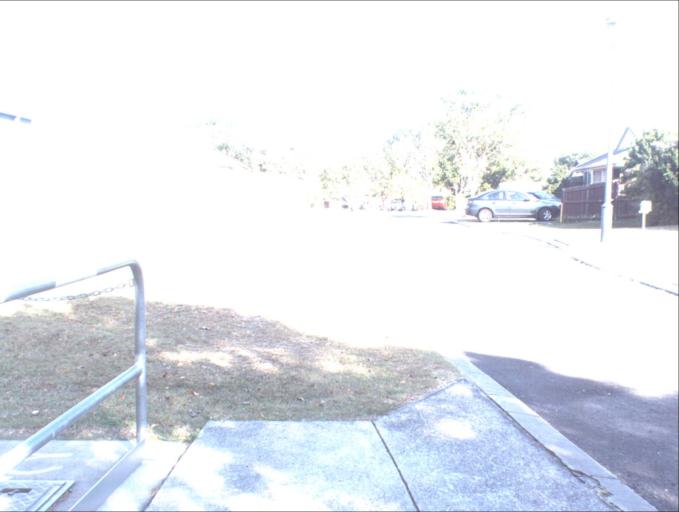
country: AU
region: Queensland
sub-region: Logan
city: Beenleigh
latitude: -27.6971
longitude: 153.1852
